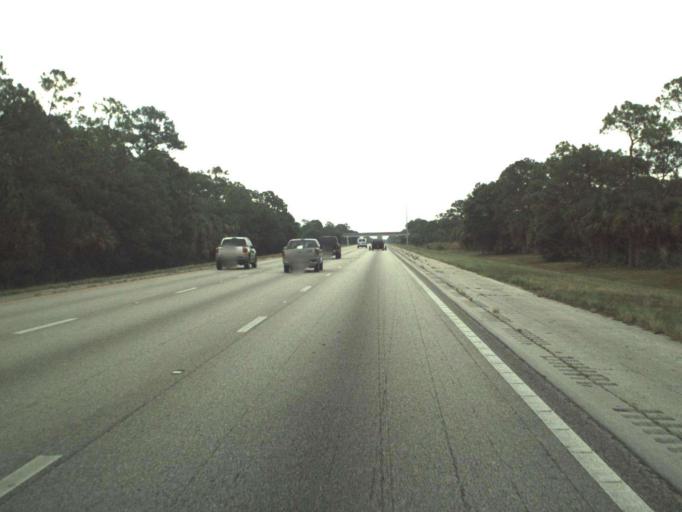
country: US
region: Florida
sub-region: Martin County
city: Palm City
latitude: 27.1267
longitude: -80.3260
